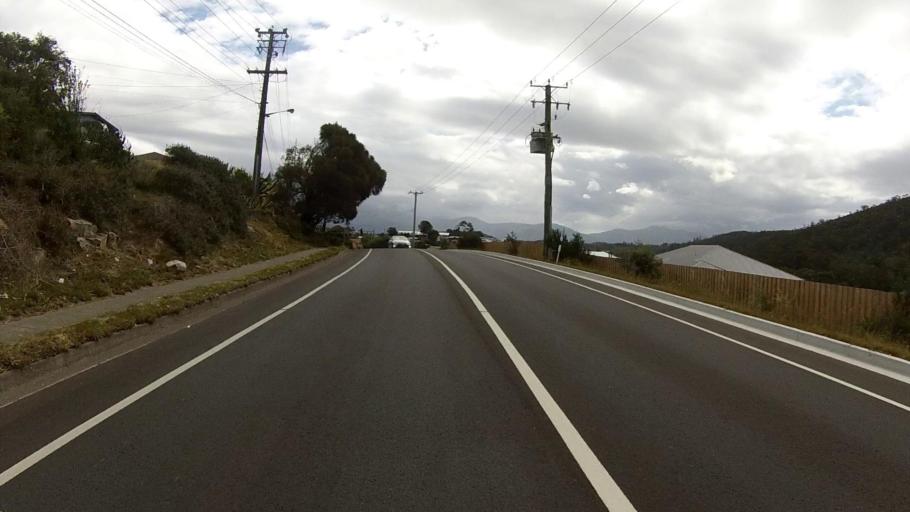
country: AU
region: Tasmania
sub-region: Clarence
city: Warrane
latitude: -42.8574
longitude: 147.4076
